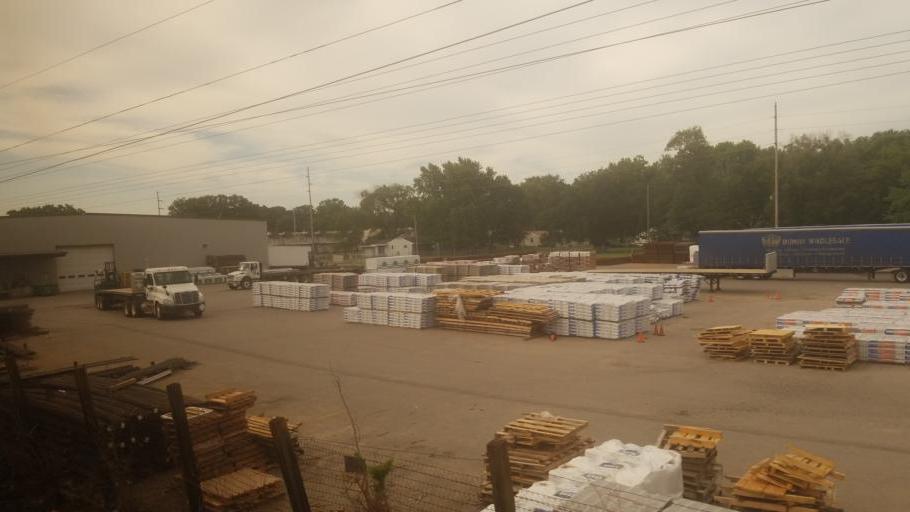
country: US
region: Kansas
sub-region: Shawnee County
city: Topeka
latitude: 39.0543
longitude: -95.6562
